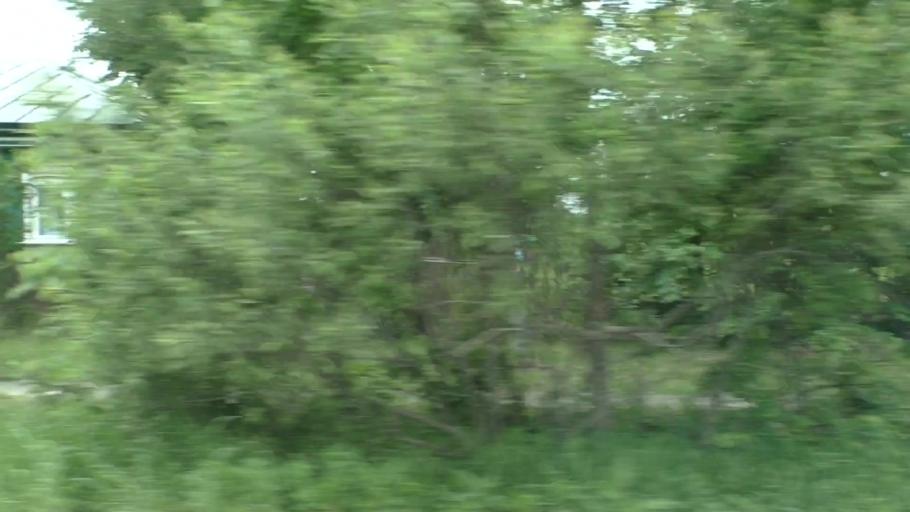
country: RU
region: Moskovskaya
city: Il'inskiy Pogost
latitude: 55.5027
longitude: 38.7932
